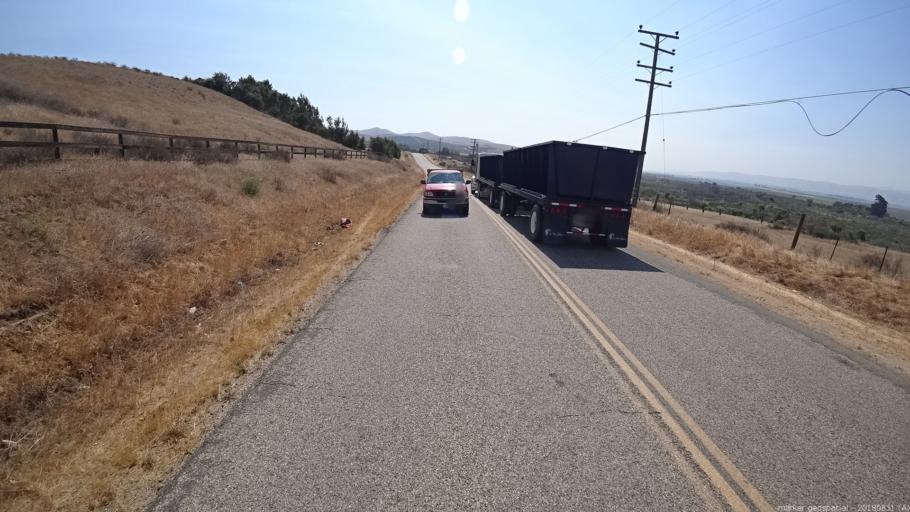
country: US
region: California
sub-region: Monterey County
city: Soledad
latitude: 36.4059
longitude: -121.2627
